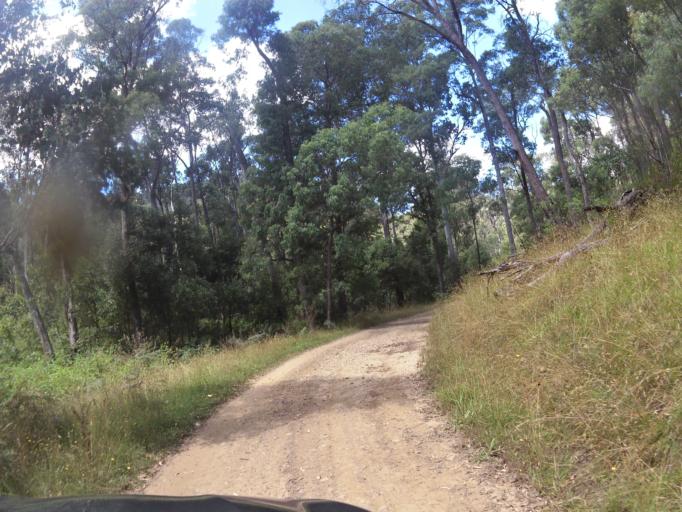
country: AU
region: Victoria
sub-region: Alpine
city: Mount Beauty
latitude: -36.7811
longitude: 147.0728
